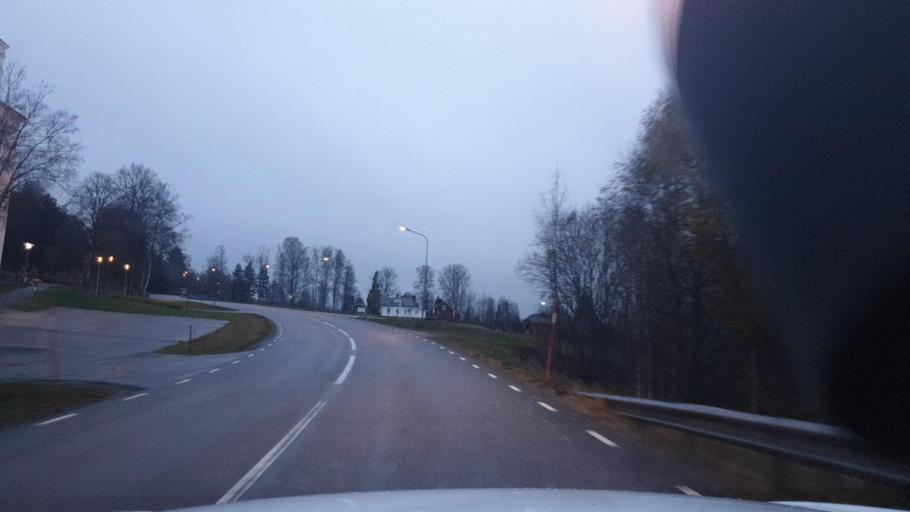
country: SE
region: Vaermland
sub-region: Eda Kommun
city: Amotfors
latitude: 59.6898
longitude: 12.1467
